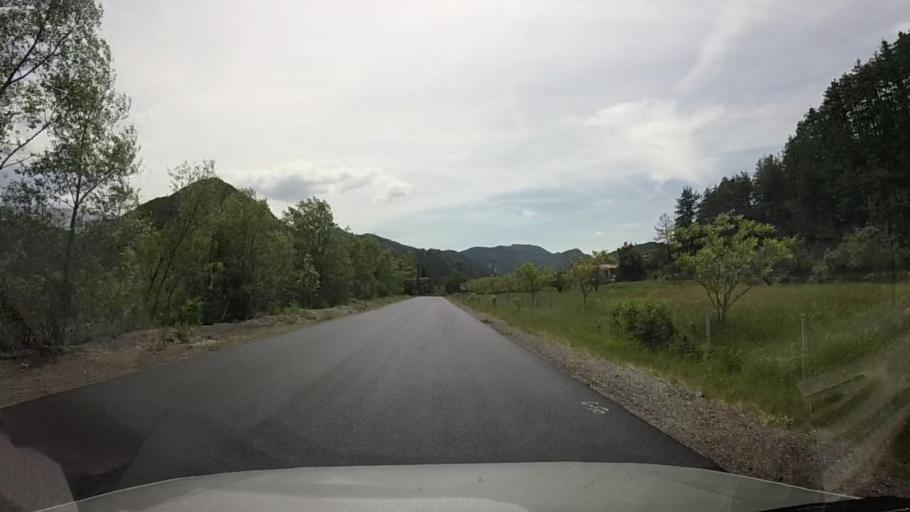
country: FR
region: Provence-Alpes-Cote d'Azur
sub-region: Departement des Alpes-de-Haute-Provence
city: Le Brusquet
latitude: 44.1922
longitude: 6.3669
